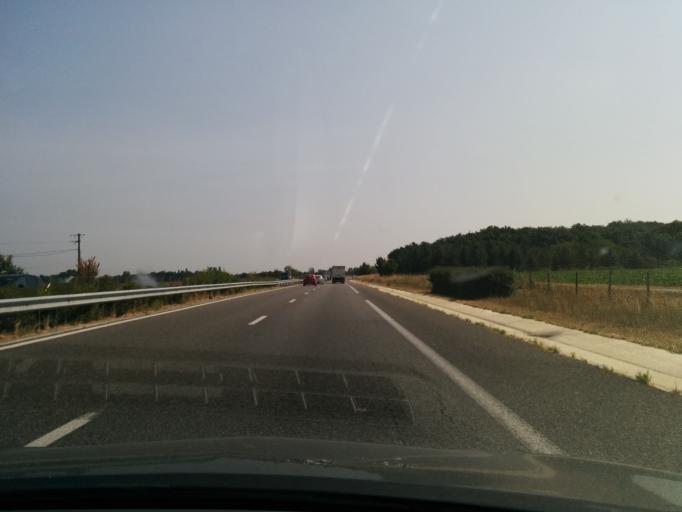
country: FR
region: Midi-Pyrenees
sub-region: Departement du Tarn
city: Giroussens
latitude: 43.8023
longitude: 1.7735
